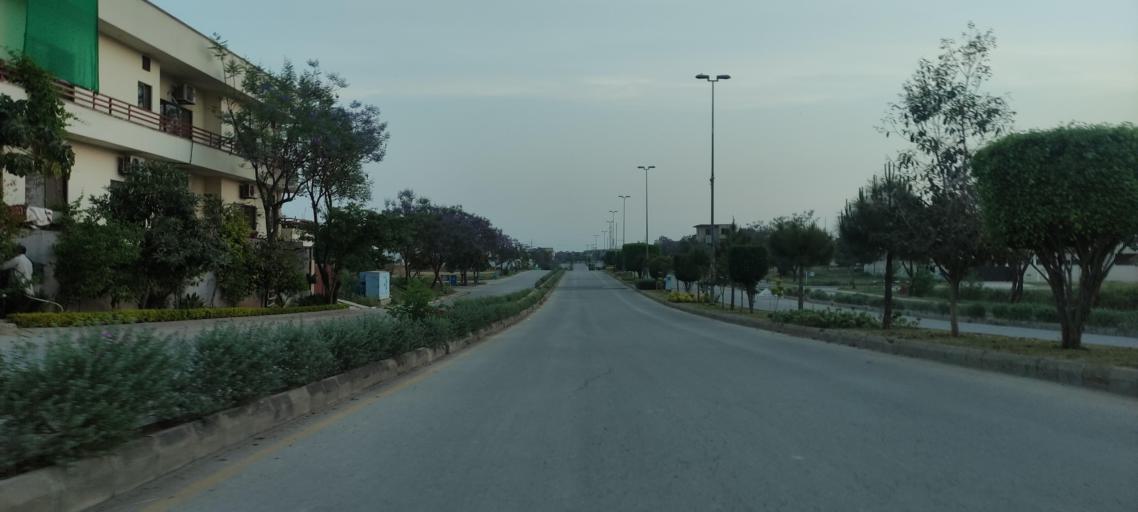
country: PK
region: Punjab
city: Rawalpindi
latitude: 33.5236
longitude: 73.1652
